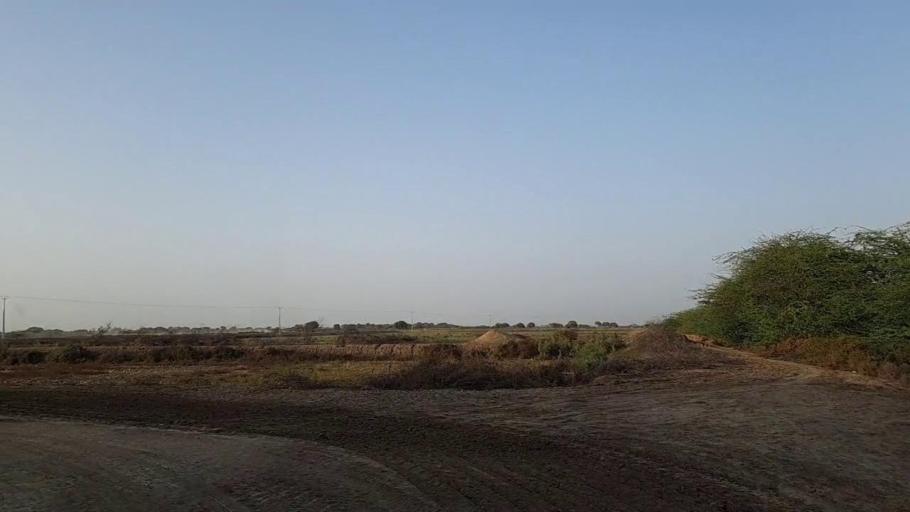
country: PK
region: Sindh
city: Jati
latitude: 24.4188
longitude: 68.1914
